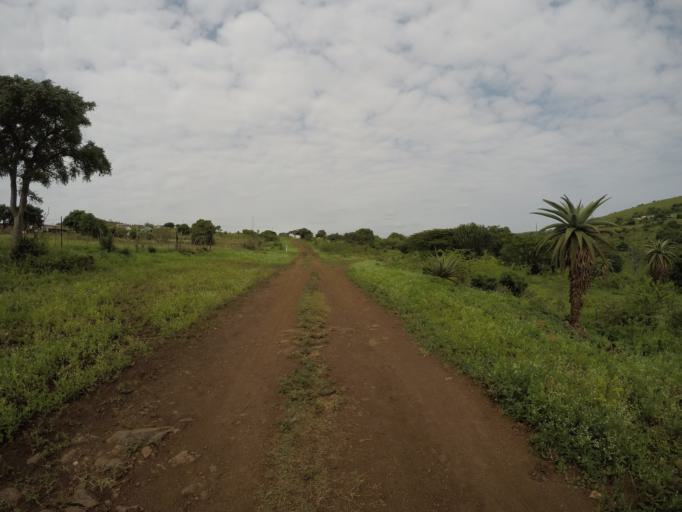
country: ZA
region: KwaZulu-Natal
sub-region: uThungulu District Municipality
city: Empangeni
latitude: -28.6278
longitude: 31.9079
